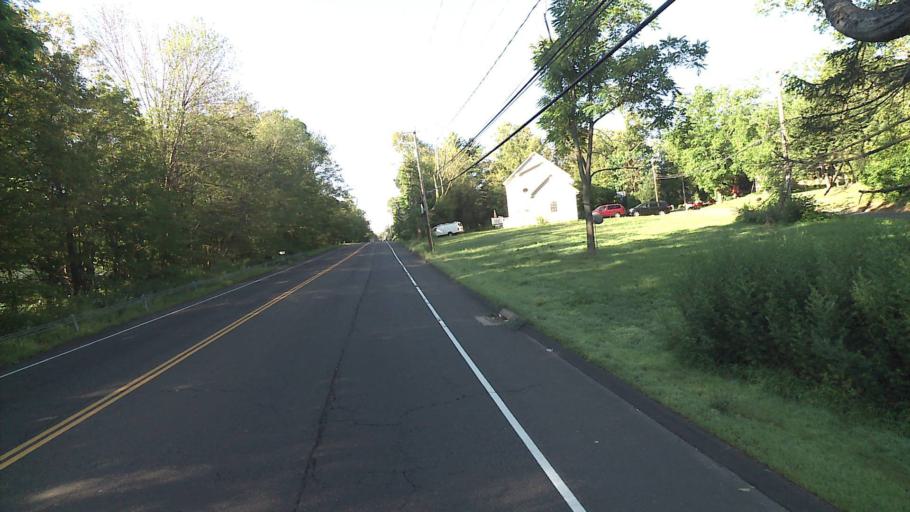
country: US
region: Connecticut
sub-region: New Haven County
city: Cheshire
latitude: 41.4665
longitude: -72.9070
